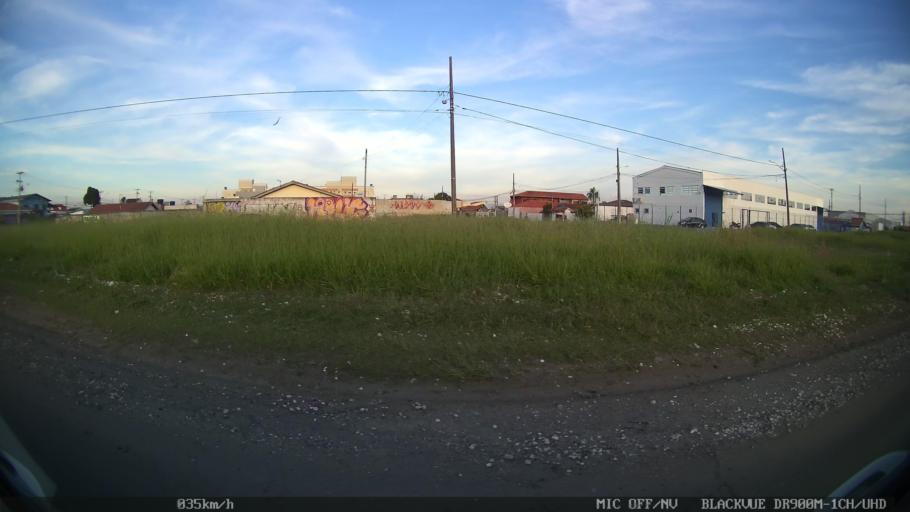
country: BR
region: Parana
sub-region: Pinhais
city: Pinhais
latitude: -25.4430
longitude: -49.1836
